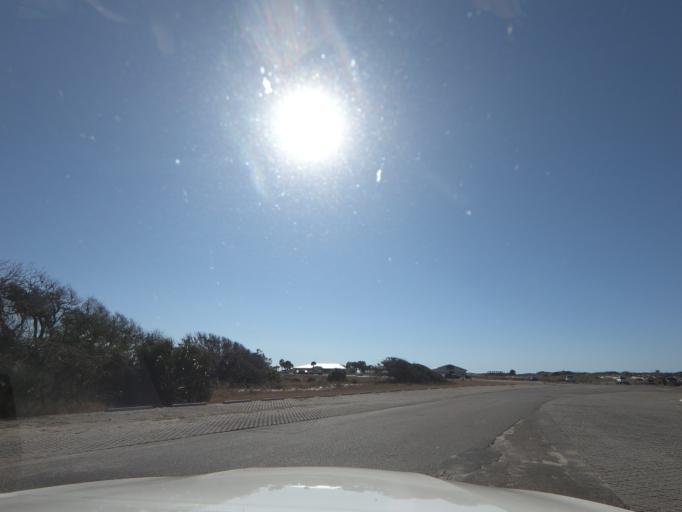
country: US
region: Florida
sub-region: Bay County
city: Lower Grand Lagoon
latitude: 30.1265
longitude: -85.7345
